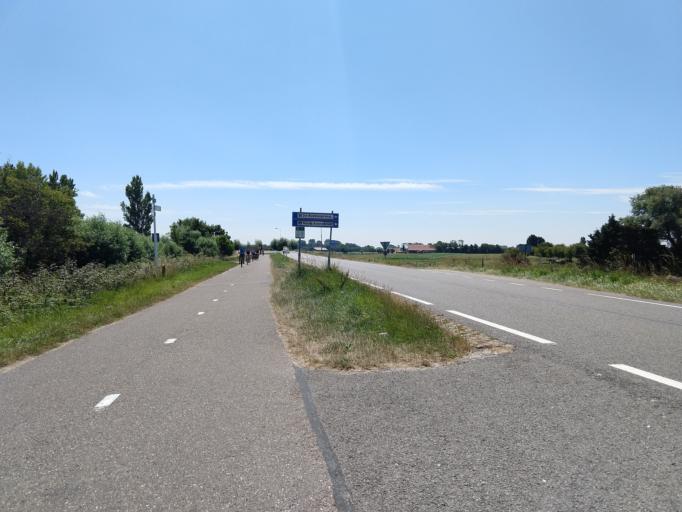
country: NL
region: Zeeland
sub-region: Gemeente Veere
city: Veere
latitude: 51.5665
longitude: 3.6321
